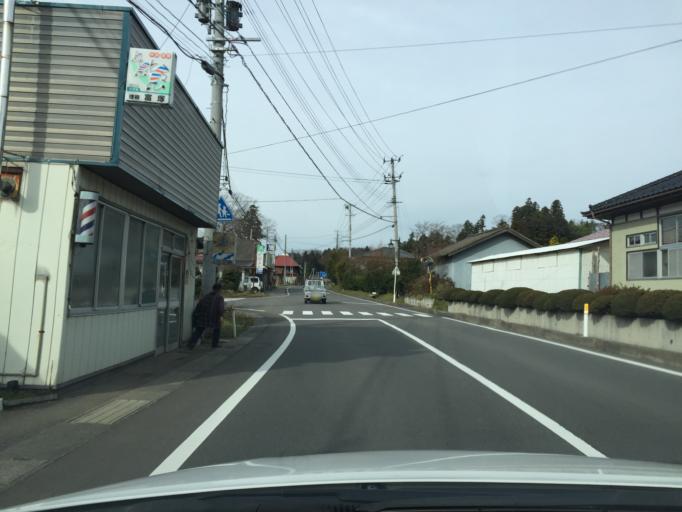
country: JP
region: Fukushima
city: Funehikimachi-funehiki
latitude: 37.3636
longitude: 140.6065
